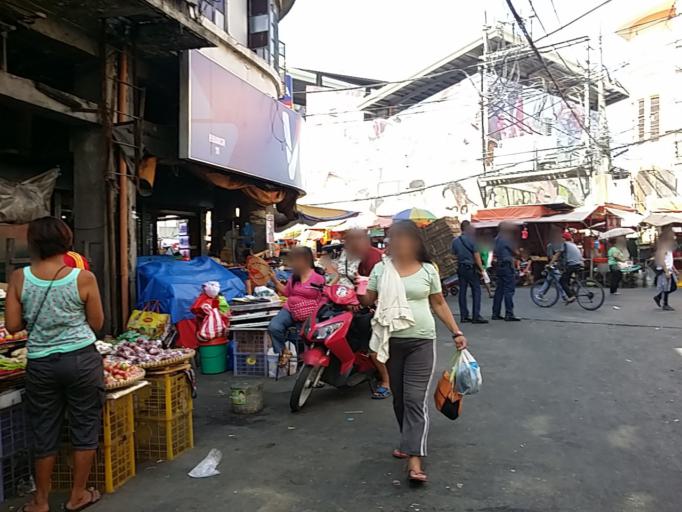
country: PH
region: Metro Manila
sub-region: City of Manila
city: Quiapo
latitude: 14.5970
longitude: 120.9830
